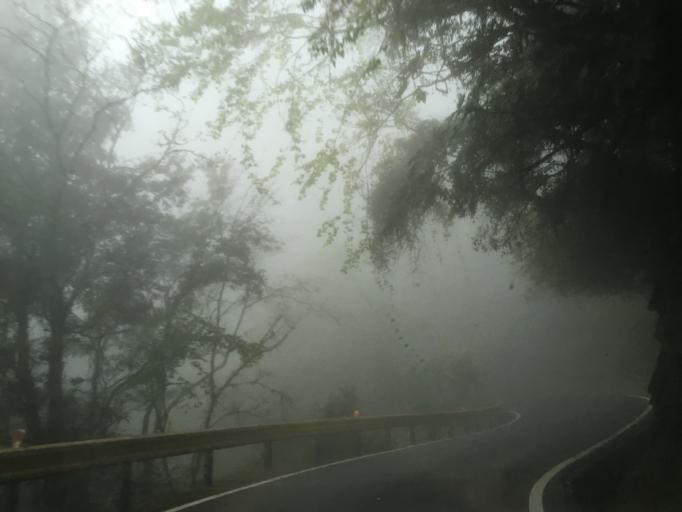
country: TW
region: Taiwan
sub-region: Hualien
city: Hualian
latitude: 24.1957
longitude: 121.4206
